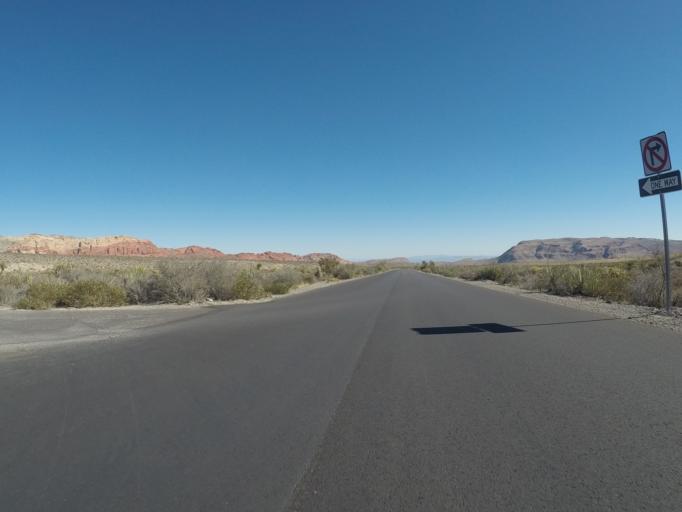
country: US
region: Nevada
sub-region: Clark County
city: Summerlin South
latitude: 36.1422
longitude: -115.4729
